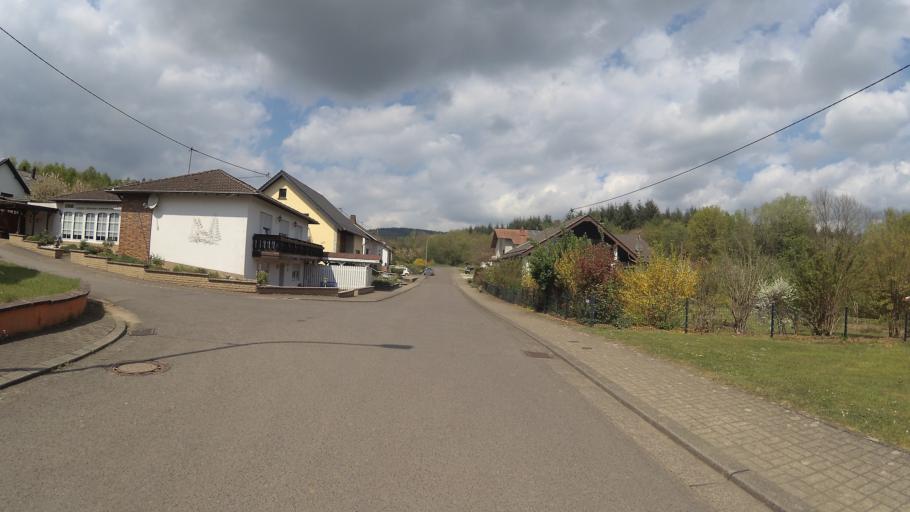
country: DE
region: Saarland
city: Weiskirchen
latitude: 49.5599
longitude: 6.8518
